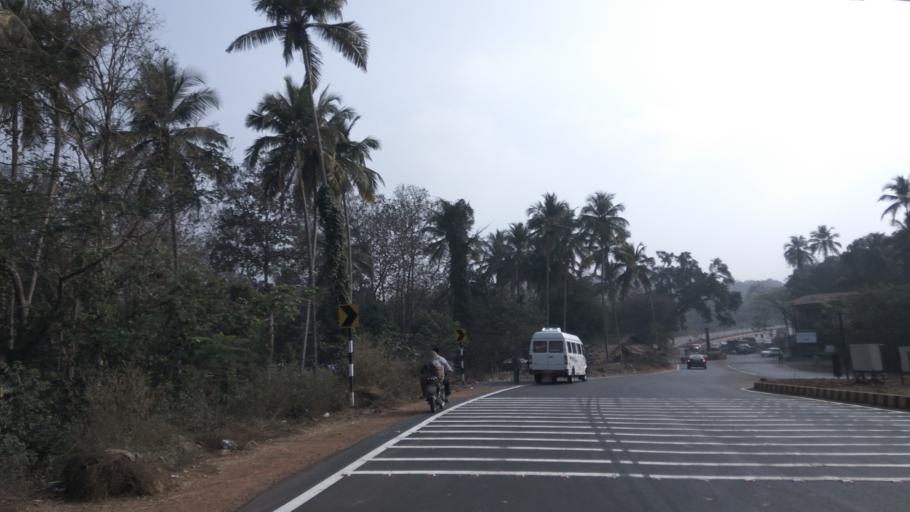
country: IN
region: Goa
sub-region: North Goa
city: Jua
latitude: 15.4989
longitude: 73.9125
